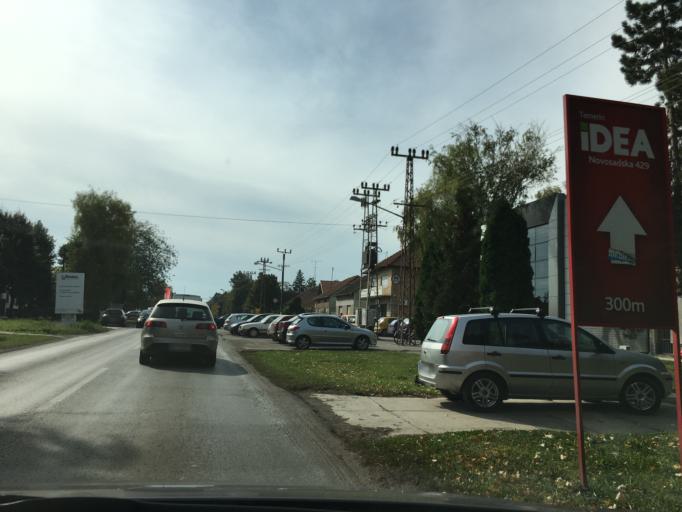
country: RS
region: Autonomna Pokrajina Vojvodina
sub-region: Juznobacki Okrug
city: Temerin
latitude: 45.4184
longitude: 19.8925
